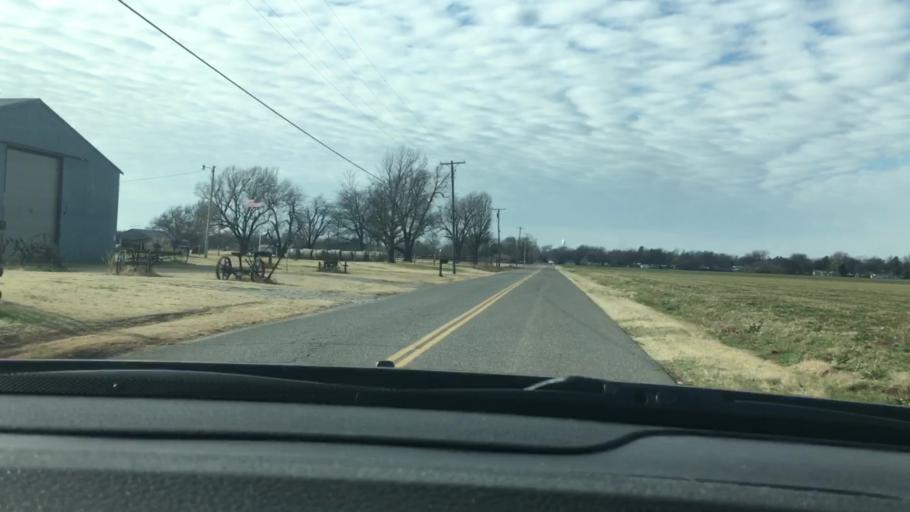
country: US
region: Oklahoma
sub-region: Garvin County
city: Pauls Valley
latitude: 34.7388
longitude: -97.1986
